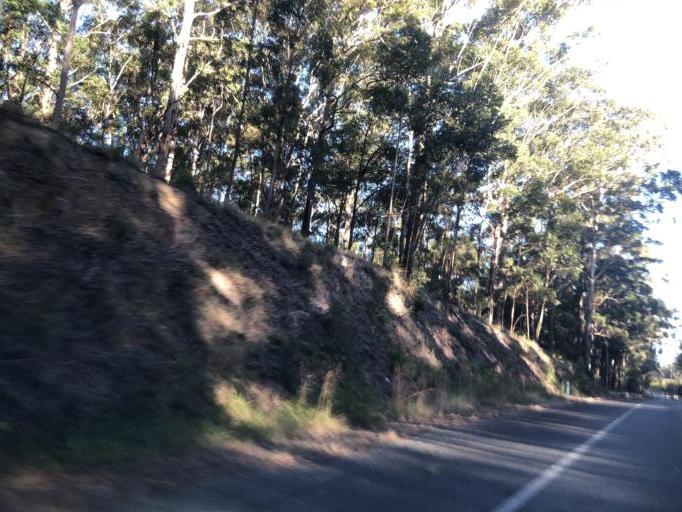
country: AU
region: New South Wales
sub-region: Nambucca Shire
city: Nambucca
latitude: -30.5537
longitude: 153.0071
